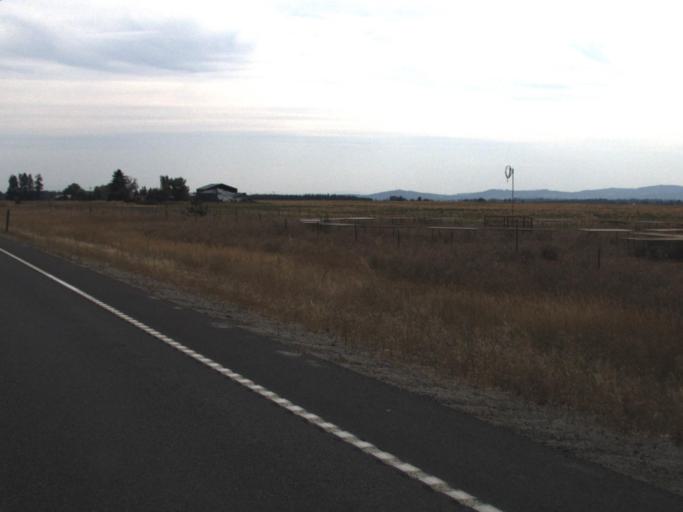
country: US
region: Washington
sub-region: Spokane County
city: Deer Park
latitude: 47.9817
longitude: -117.5282
